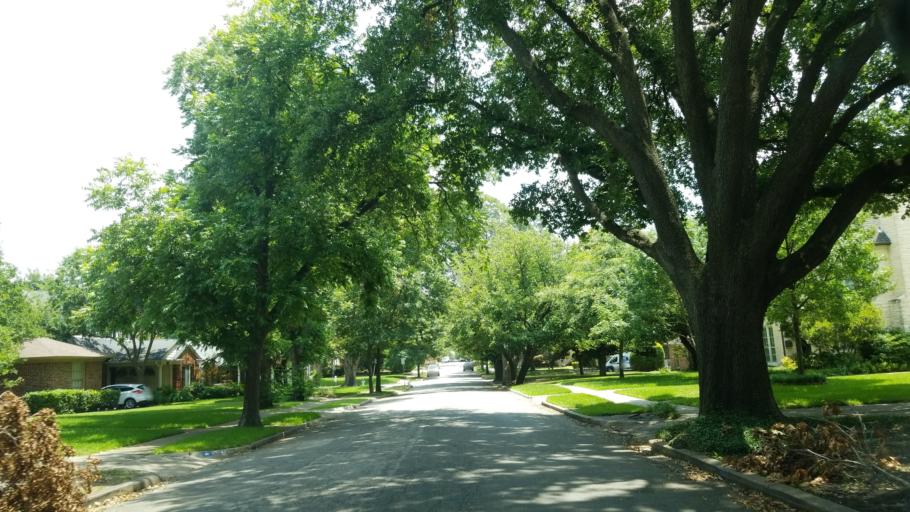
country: US
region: Texas
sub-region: Dallas County
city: Highland Park
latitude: 32.8260
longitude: -96.7646
